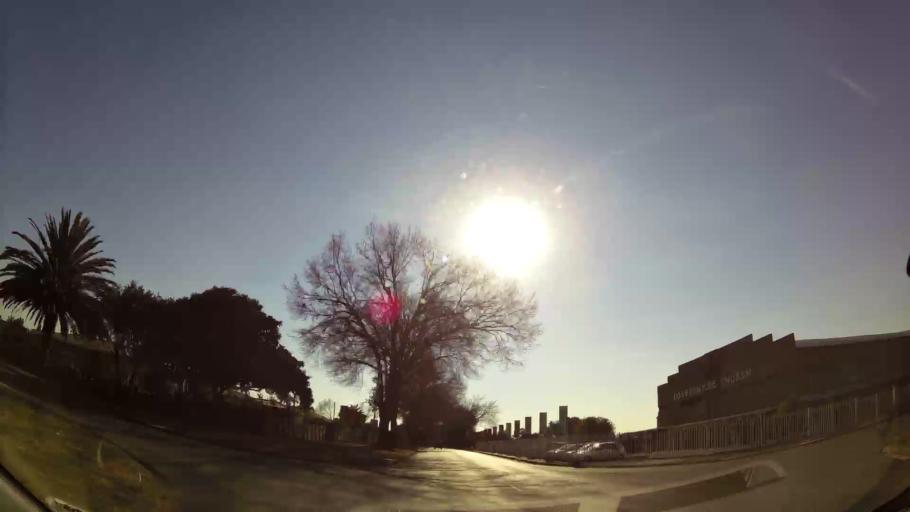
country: ZA
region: Gauteng
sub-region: Ekurhuleni Metropolitan Municipality
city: Benoni
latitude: -26.1622
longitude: 28.3143
